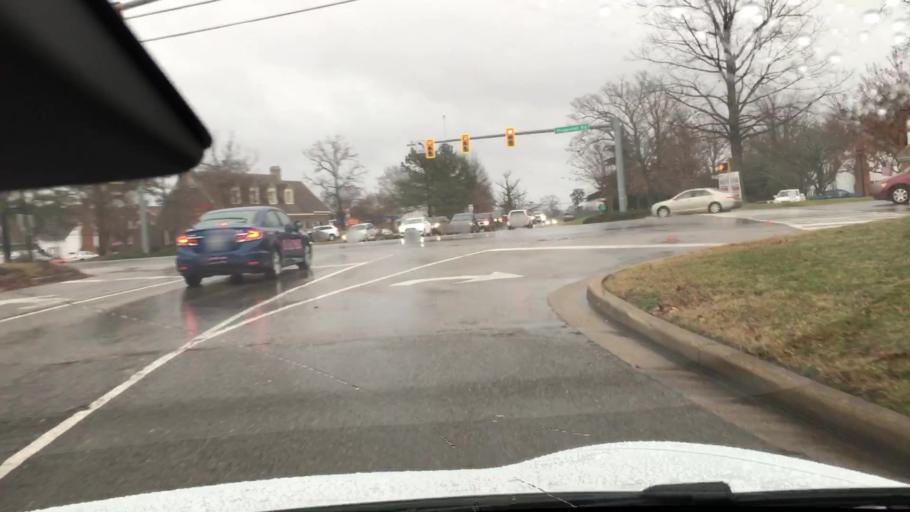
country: US
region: Virginia
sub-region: Chesterfield County
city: Bon Air
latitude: 37.5363
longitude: -77.5651
